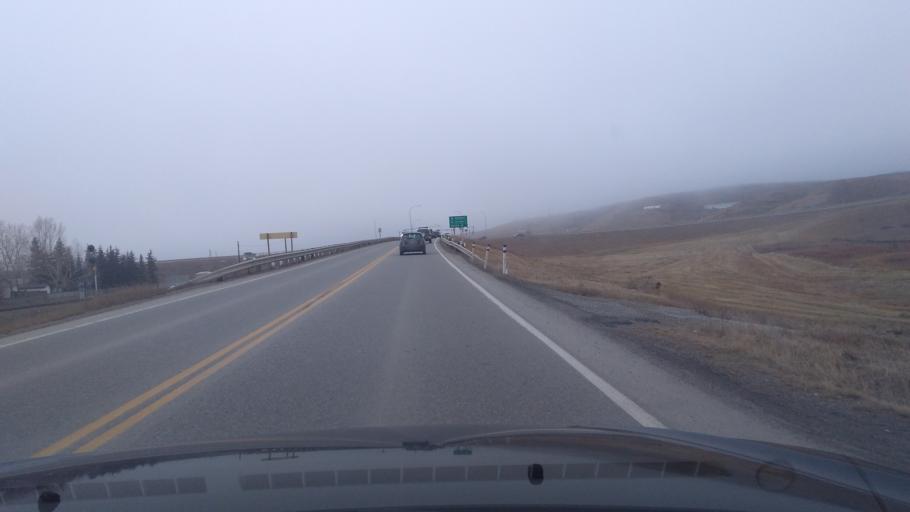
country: CA
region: Alberta
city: Cochrane
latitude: 51.1964
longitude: -114.4827
